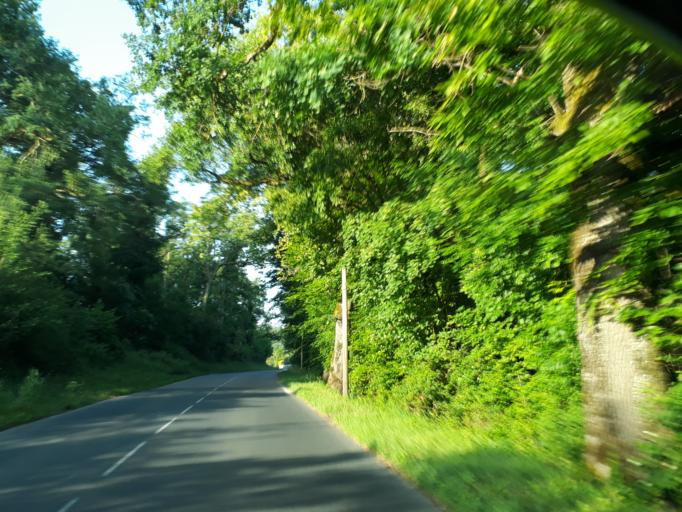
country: FR
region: Limousin
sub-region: Departement de la Correze
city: Saint-Pantaleon-de-Larche
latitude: 45.1189
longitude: 1.4658
